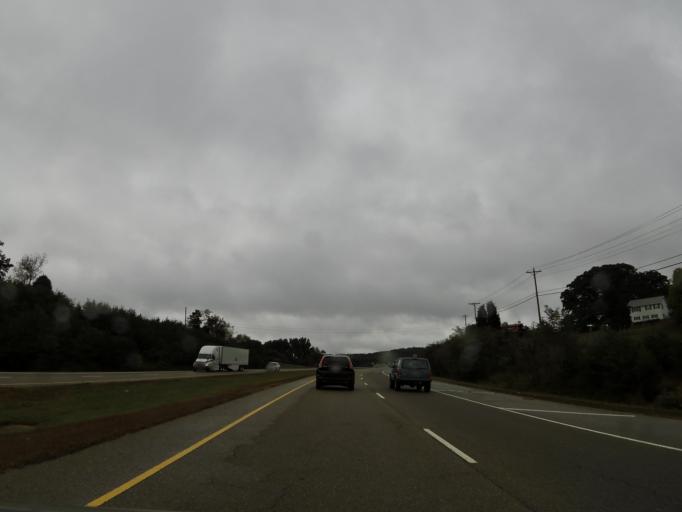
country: US
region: Tennessee
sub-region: Loudon County
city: Lenoir City
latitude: 35.7451
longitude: -84.2137
